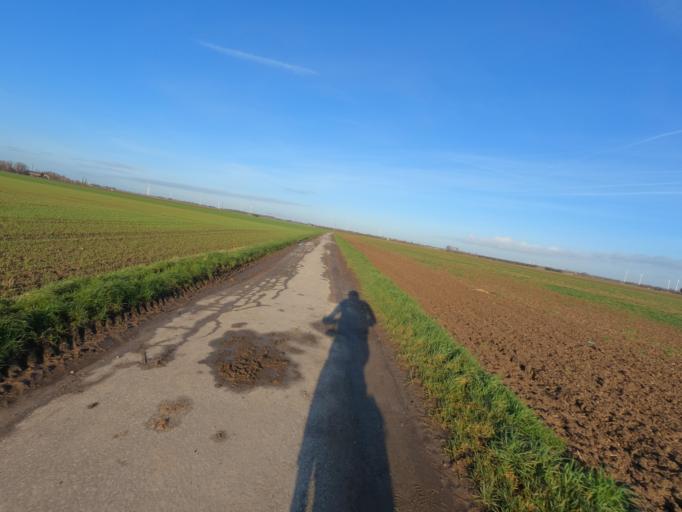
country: DE
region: North Rhine-Westphalia
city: Julich
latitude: 50.9345
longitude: 6.4007
